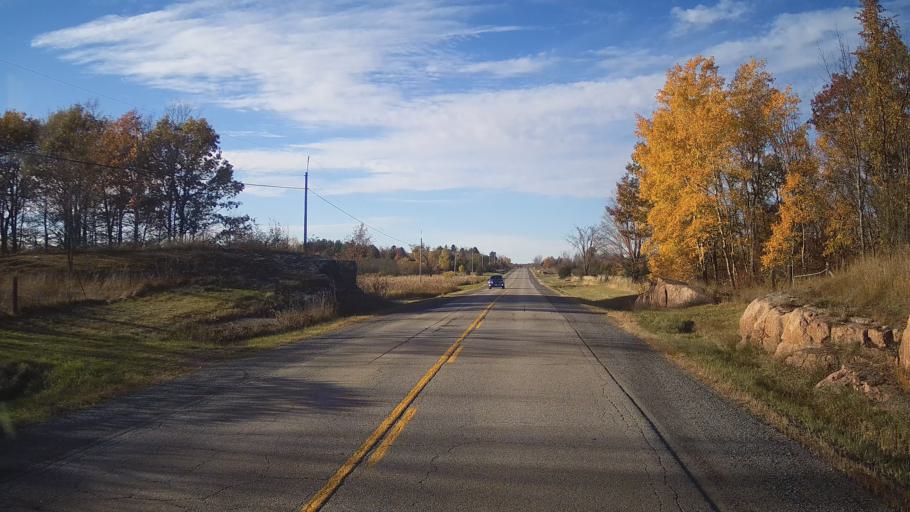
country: CA
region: Ontario
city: Perth
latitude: 44.7086
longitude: -76.4330
